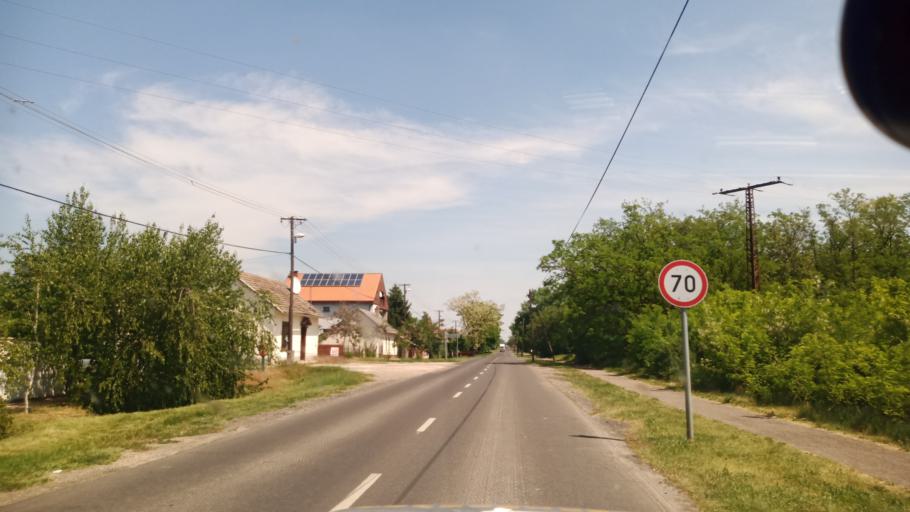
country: HU
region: Bekes
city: Oroshaza
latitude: 46.5650
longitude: 20.5990
